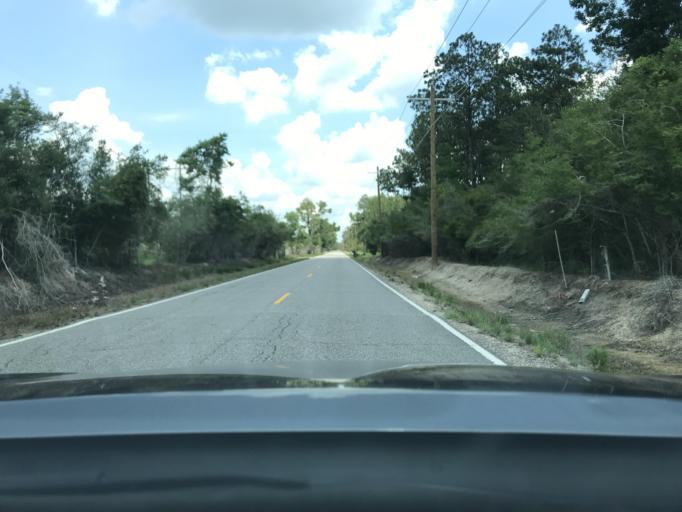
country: US
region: Louisiana
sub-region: Calcasieu Parish
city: Moss Bluff
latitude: 30.3300
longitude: -93.1657
